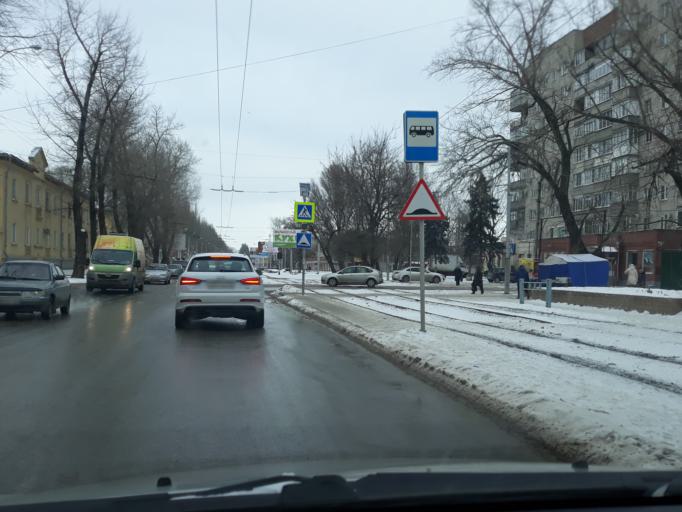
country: RU
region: Rostov
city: Taganrog
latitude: 47.2395
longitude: 38.9173
